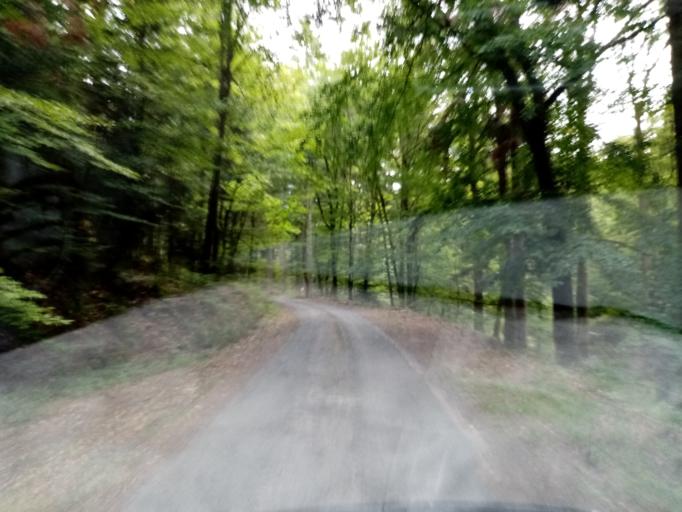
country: FR
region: Alsace
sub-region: Departement du Bas-Rhin
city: Dambach-la-Ville
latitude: 48.3408
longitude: 7.3893
